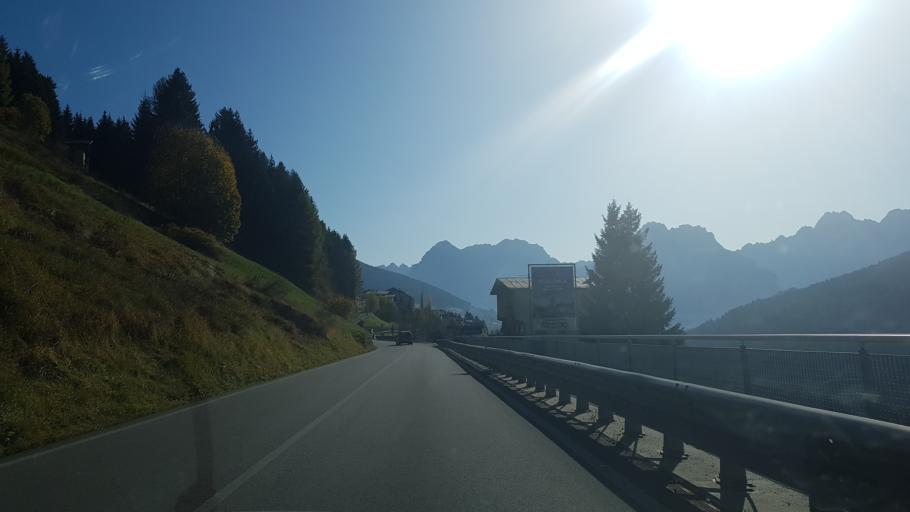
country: IT
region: Veneto
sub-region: Provincia di Belluno
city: Candide
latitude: 46.5930
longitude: 12.5041
